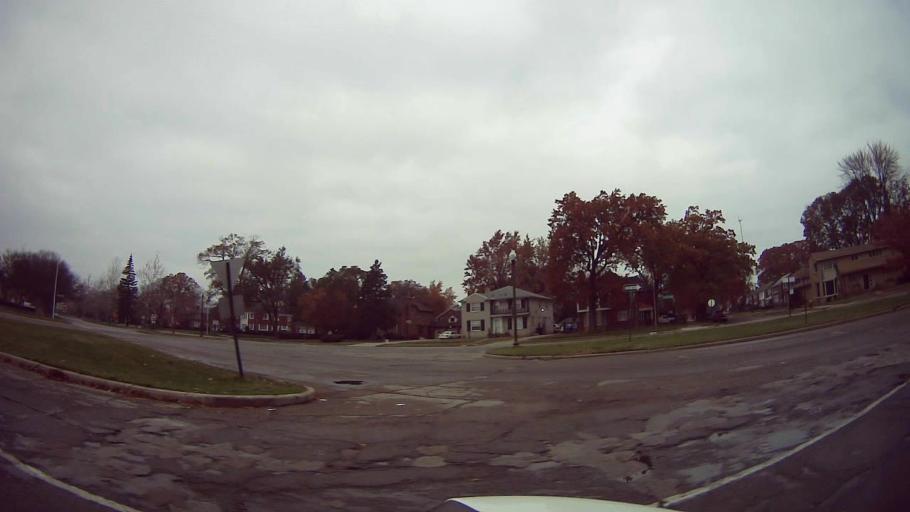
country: US
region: Michigan
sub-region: Oakland County
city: Oak Park
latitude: 42.4340
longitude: -83.1752
